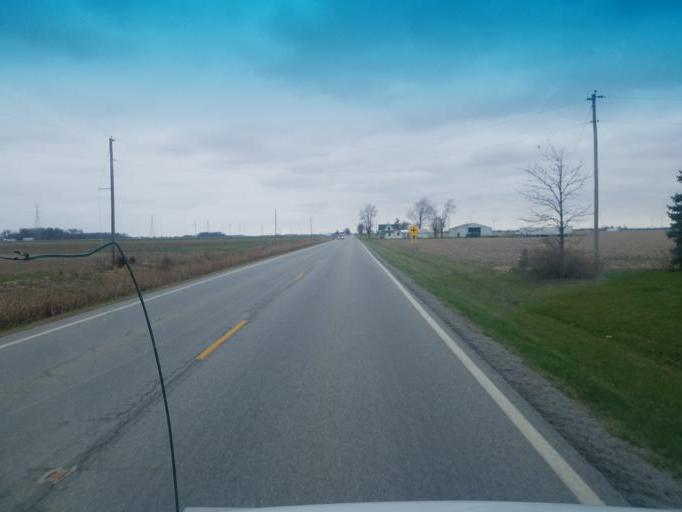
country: US
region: Ohio
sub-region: Van Wert County
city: Van Wert
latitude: 40.9321
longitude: -84.4707
